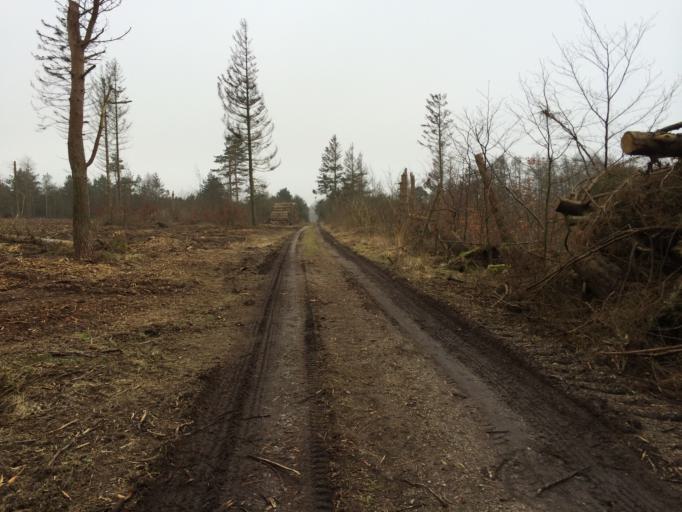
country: DK
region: Central Jutland
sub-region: Lemvig Kommune
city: Lemvig
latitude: 56.5047
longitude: 8.3014
